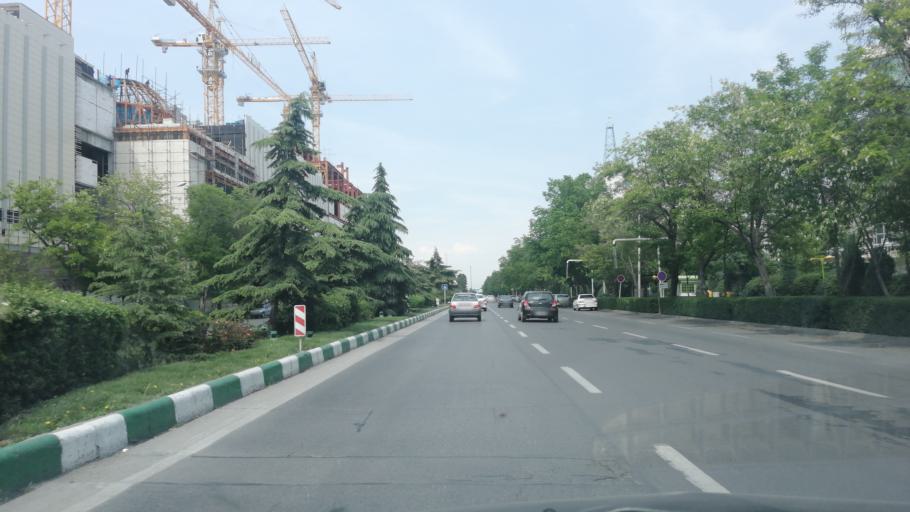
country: IR
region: Razavi Khorasan
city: Mashhad
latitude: 36.3158
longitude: 59.5614
